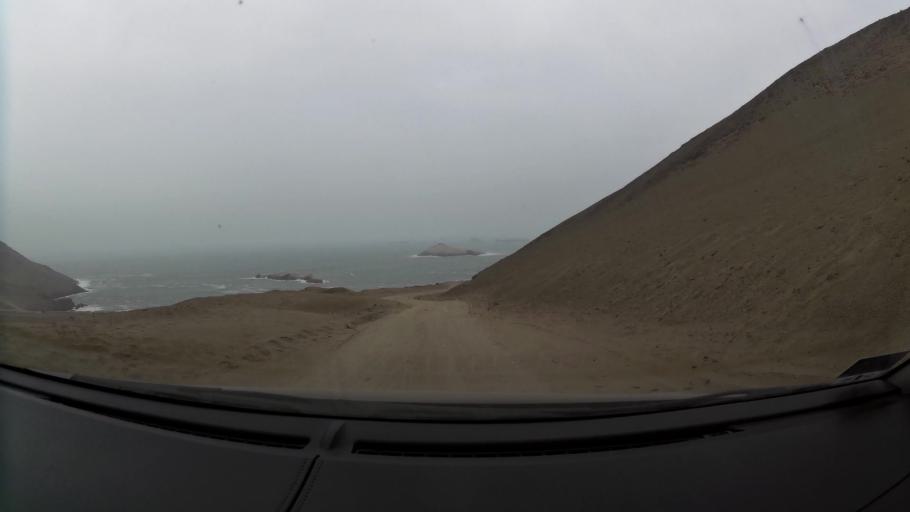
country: PE
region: Lima
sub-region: Lima
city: Santa Rosa
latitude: -11.8125
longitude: -77.1714
